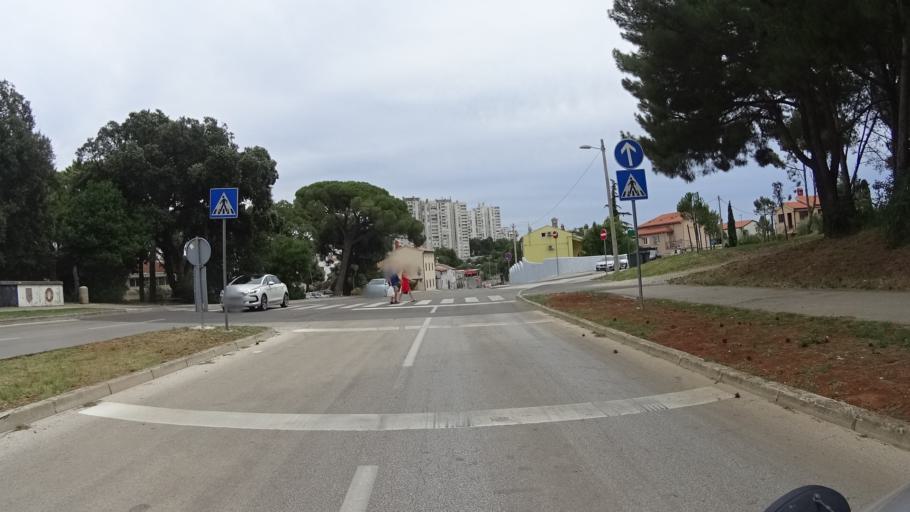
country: HR
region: Istarska
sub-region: Grad Pula
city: Pula
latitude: 44.8560
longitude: 13.8360
